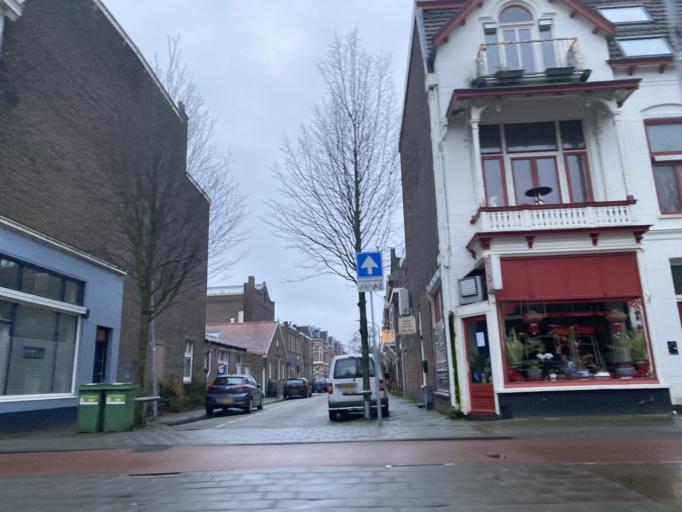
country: NL
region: North Holland
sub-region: Gemeente Haarlem
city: Haarlem
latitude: 52.3851
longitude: 4.6249
